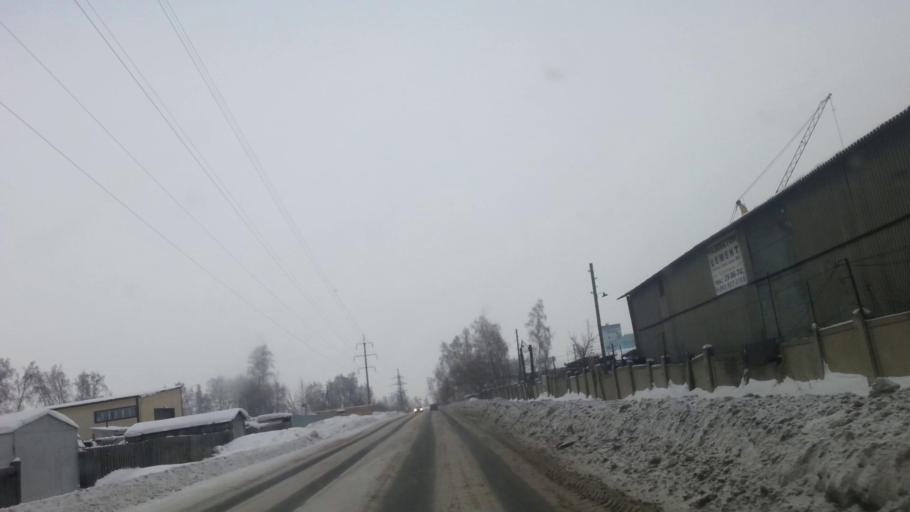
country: RU
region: Altai Krai
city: Novosilikatnyy
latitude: 53.3121
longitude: 83.6184
